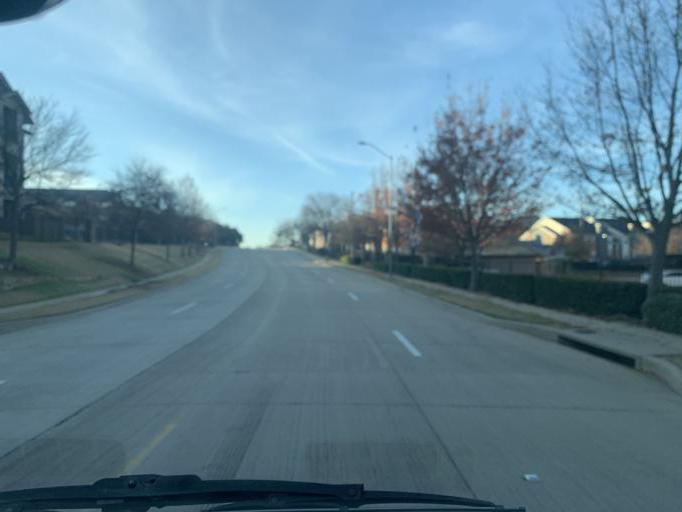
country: US
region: Texas
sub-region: Tarrant County
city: Euless
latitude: 32.7908
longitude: -97.0625
